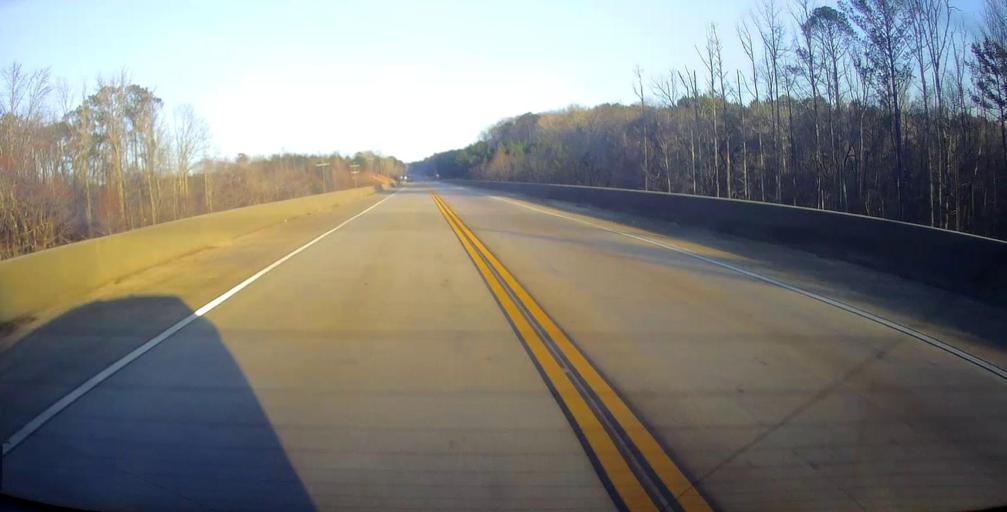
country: US
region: Georgia
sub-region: Troup County
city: La Grange
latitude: 32.9897
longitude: -85.0607
